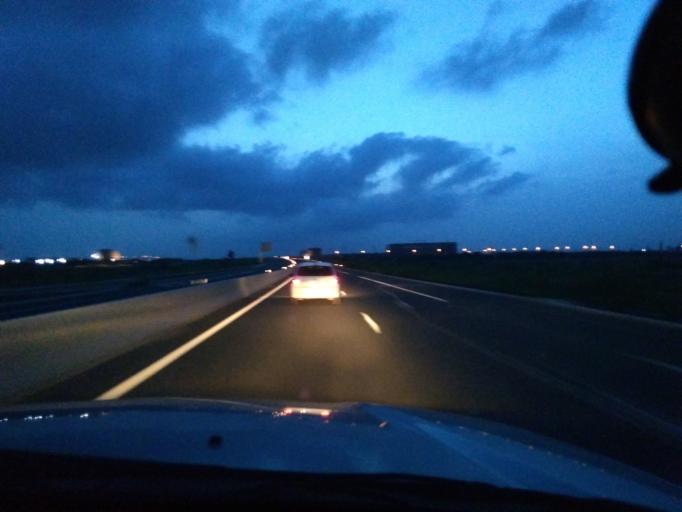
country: SN
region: Thies
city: Thies
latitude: 14.7332
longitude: -17.2058
